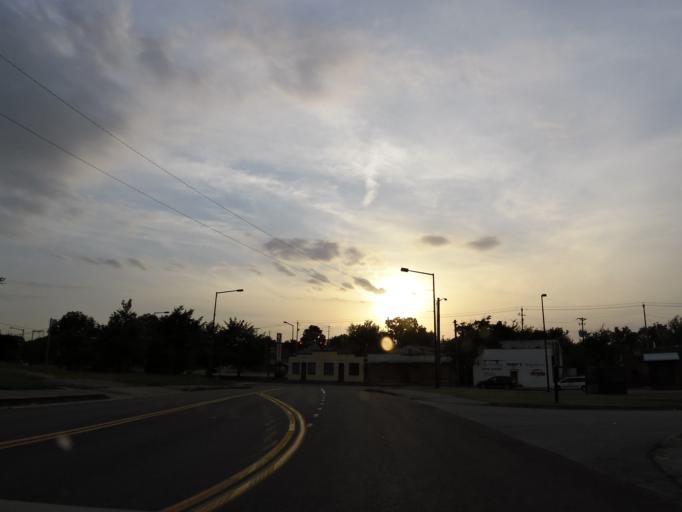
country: US
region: Tennessee
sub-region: Knox County
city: Knoxville
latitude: 35.9802
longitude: -83.8959
